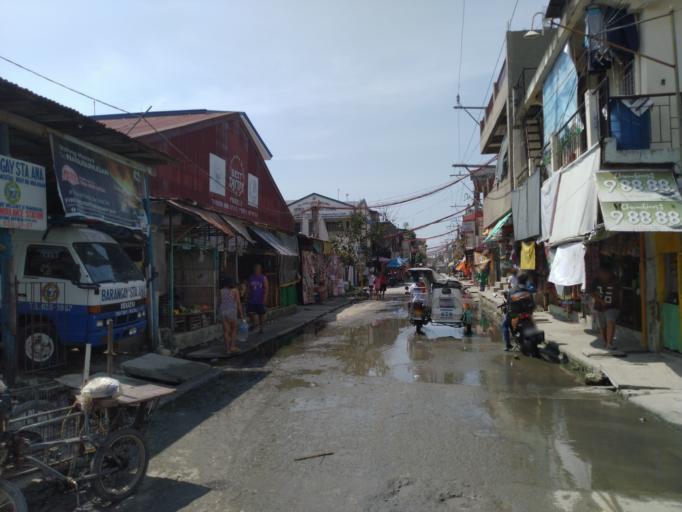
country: PH
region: Calabarzon
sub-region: Province of Rizal
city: Taytay
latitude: 14.5402
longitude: 121.1111
